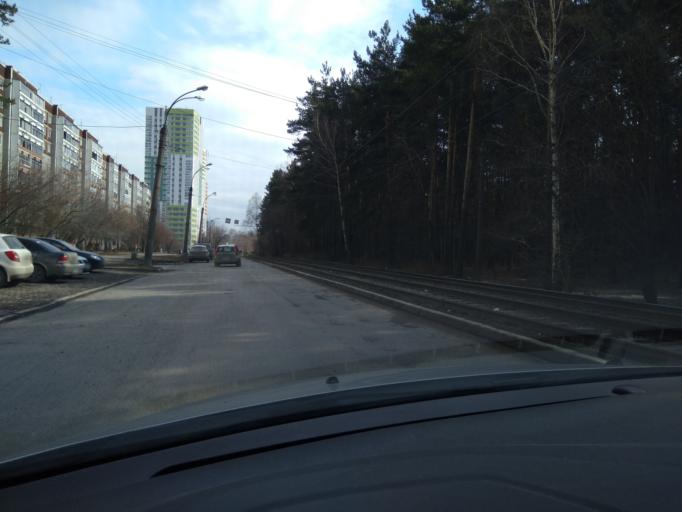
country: RU
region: Sverdlovsk
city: Shuvakish
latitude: 56.8823
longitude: 60.5014
